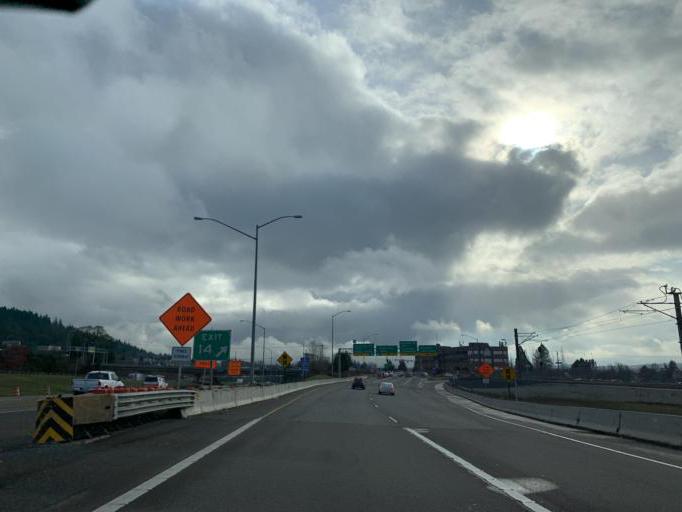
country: US
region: Oregon
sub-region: Clackamas County
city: Clackamas
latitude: 45.4355
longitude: -122.5674
